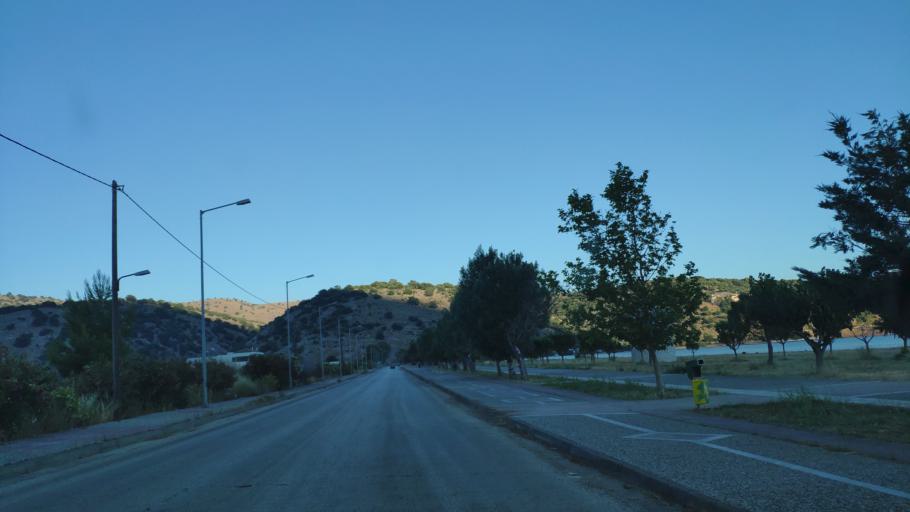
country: GR
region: West Greece
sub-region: Nomos Aitolias kai Akarnanias
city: Astakos
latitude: 38.5346
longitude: 21.0912
